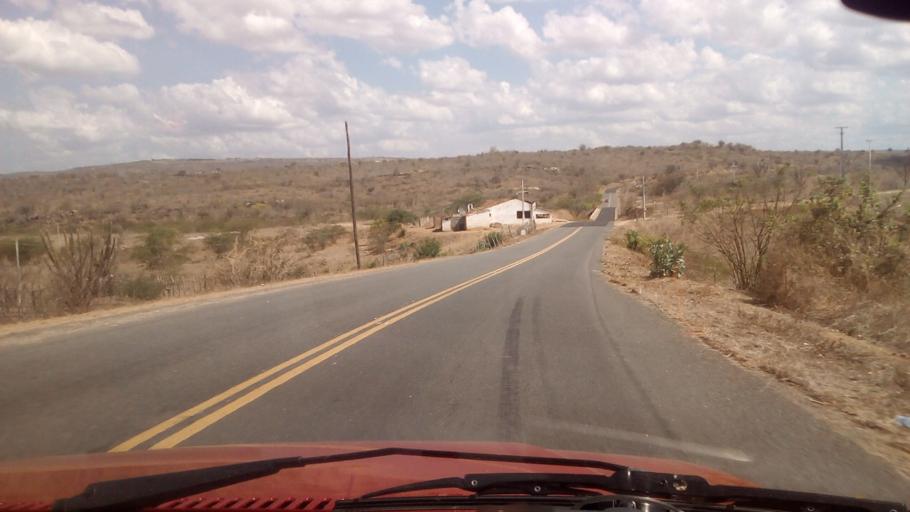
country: BR
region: Paraiba
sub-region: Cacimba De Dentro
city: Cacimba de Dentro
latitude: -6.6755
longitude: -35.7458
